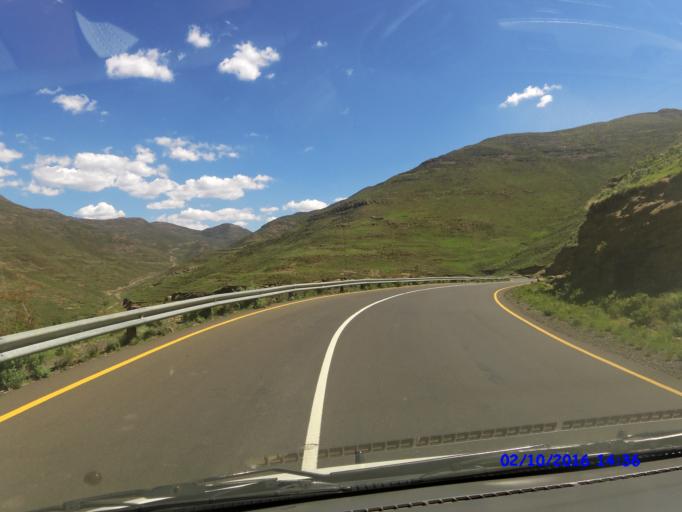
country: LS
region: Maseru
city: Nako
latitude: -29.4984
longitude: 28.0628
